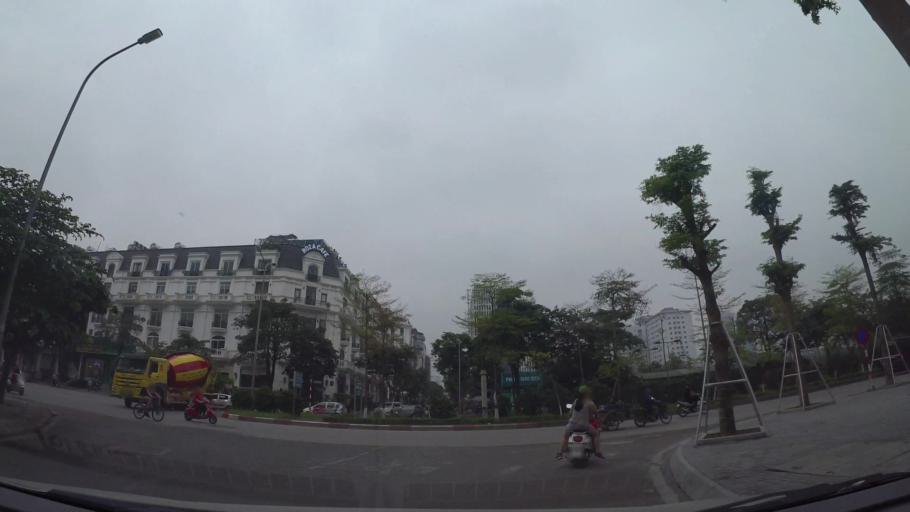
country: VN
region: Ha Noi
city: Cau Giay
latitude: 21.0276
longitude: 105.7858
